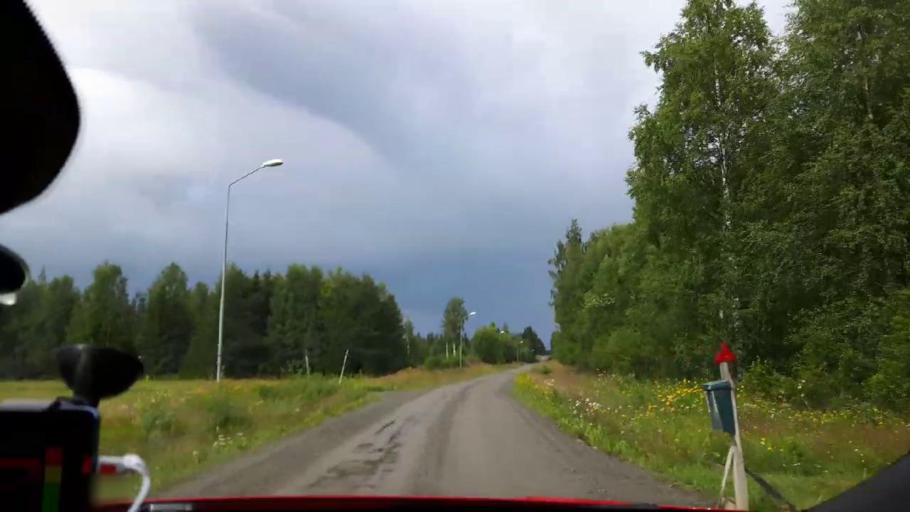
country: SE
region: Jaemtland
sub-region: Stroemsunds Kommun
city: Stroemsund
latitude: 64.0583
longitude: 15.8902
